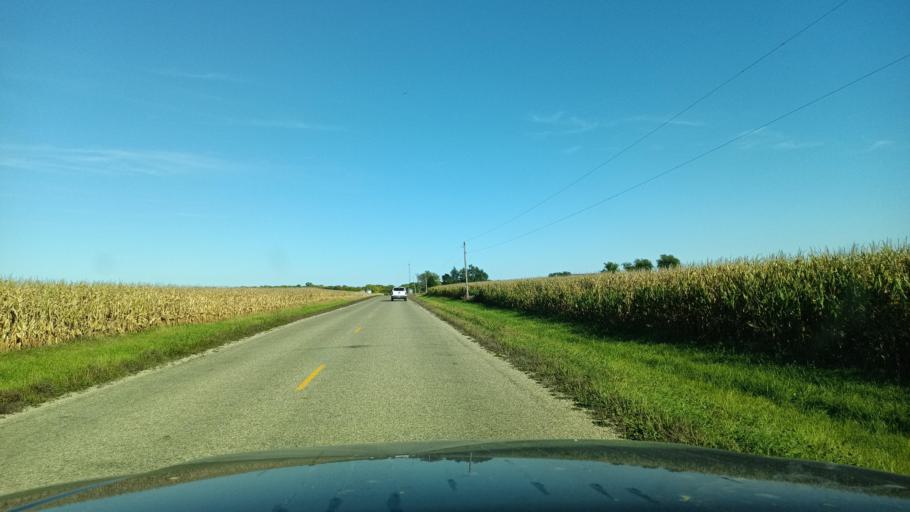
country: US
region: Illinois
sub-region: Logan County
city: Atlanta
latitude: 40.2344
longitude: -89.1429
